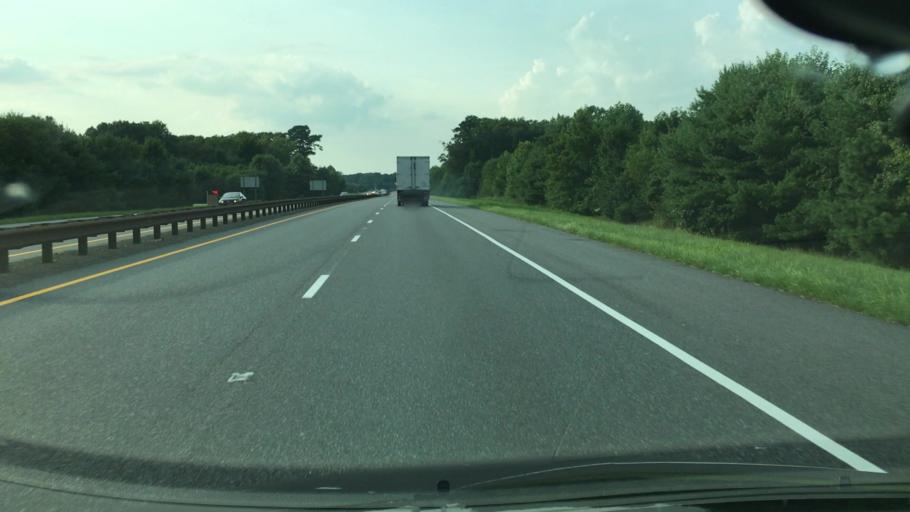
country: US
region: Maryland
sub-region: Worcester County
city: Ocean Pines
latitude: 38.3986
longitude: -75.2074
